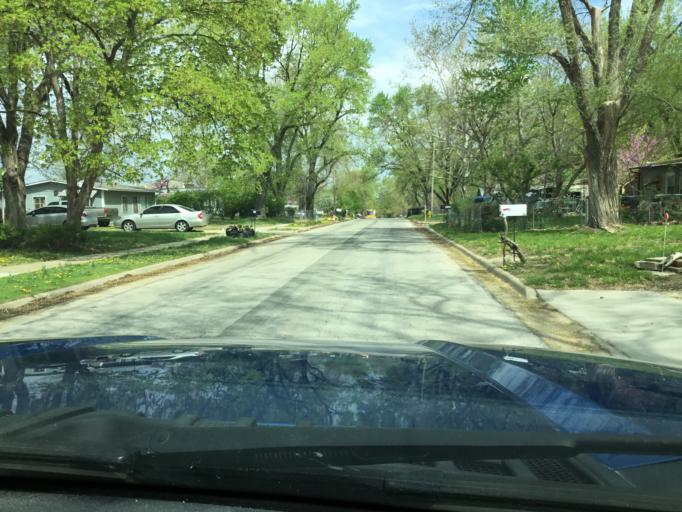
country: US
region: Kansas
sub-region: Douglas County
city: Lawrence
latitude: 38.9543
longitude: -95.2137
